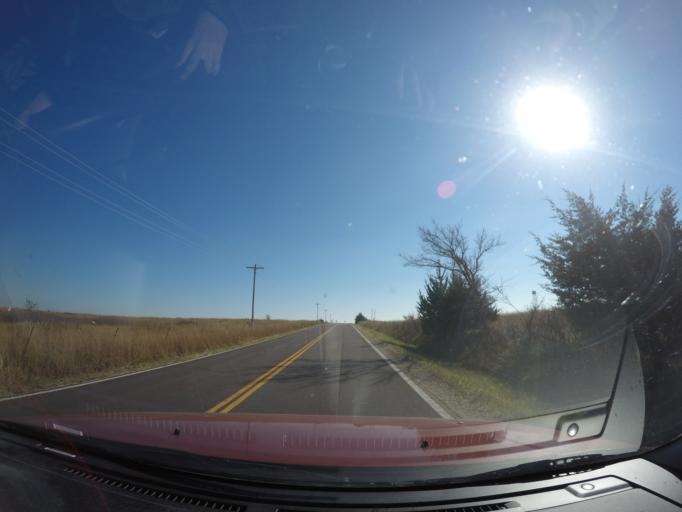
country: US
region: Kansas
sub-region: Geary County
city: Grandview Plaza
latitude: 39.0238
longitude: -96.7642
